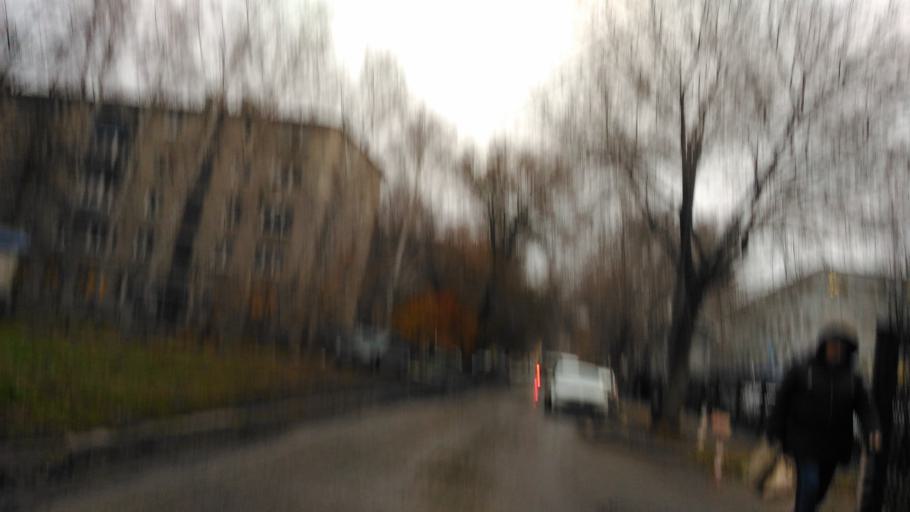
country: RU
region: Ulyanovsk
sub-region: Ulyanovskiy Rayon
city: Ulyanovsk
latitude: 54.3003
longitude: 48.3274
